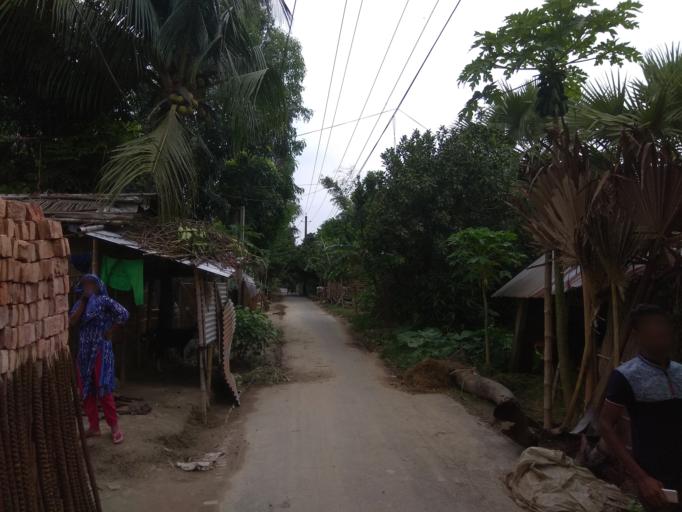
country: BD
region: Dhaka
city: Dohar
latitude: 23.4865
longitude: 90.0276
